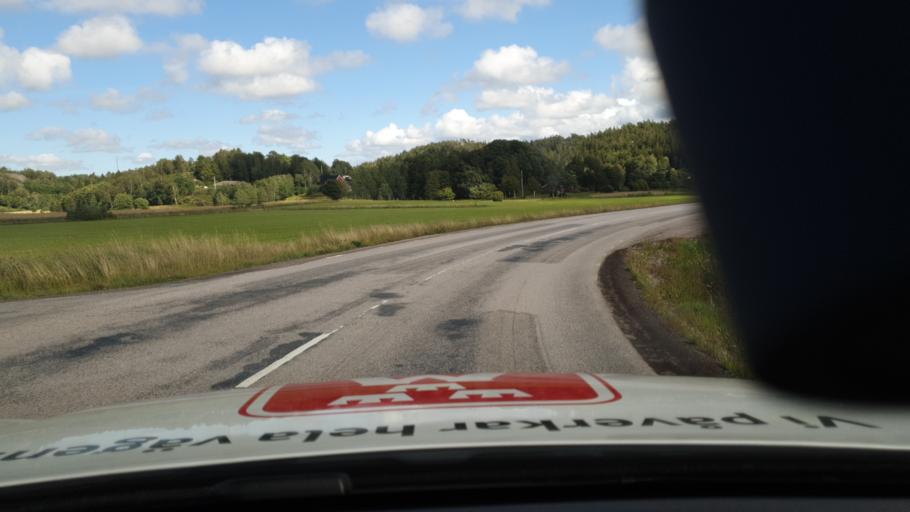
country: SE
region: Vaestra Goetaland
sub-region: Orust
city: Henan
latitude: 58.2277
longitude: 11.6365
